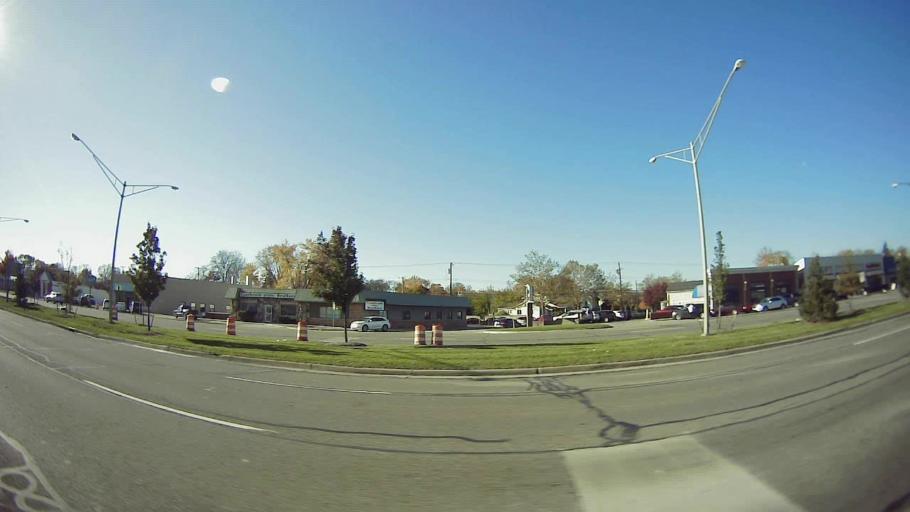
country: US
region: Michigan
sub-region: Oakland County
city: Birmingham
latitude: 42.5370
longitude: -83.2044
